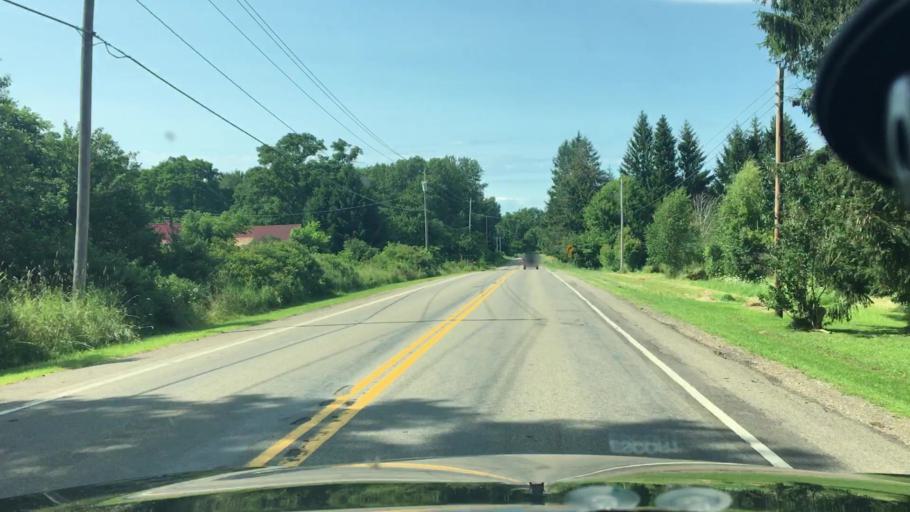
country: US
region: New York
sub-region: Chautauqua County
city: Brocton
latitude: 42.2681
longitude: -79.3514
